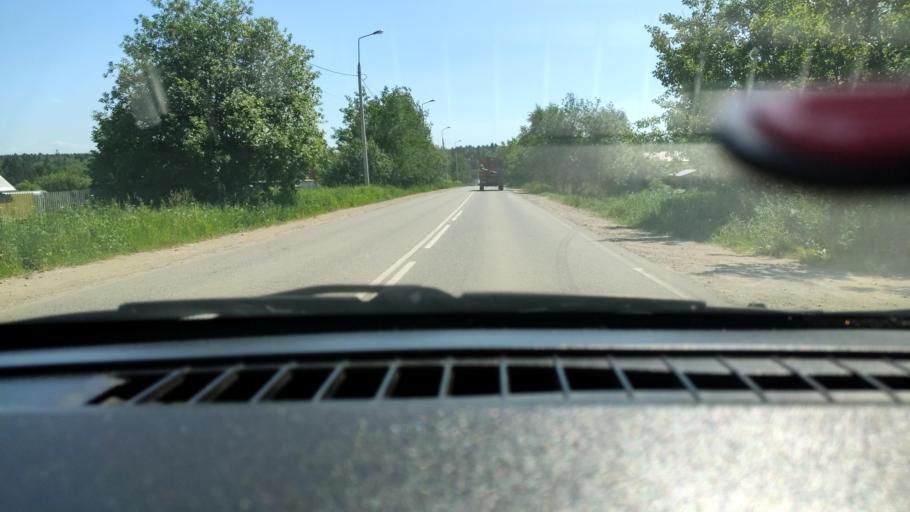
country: RU
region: Perm
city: Novyye Lyady
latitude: 58.0433
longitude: 56.5954
